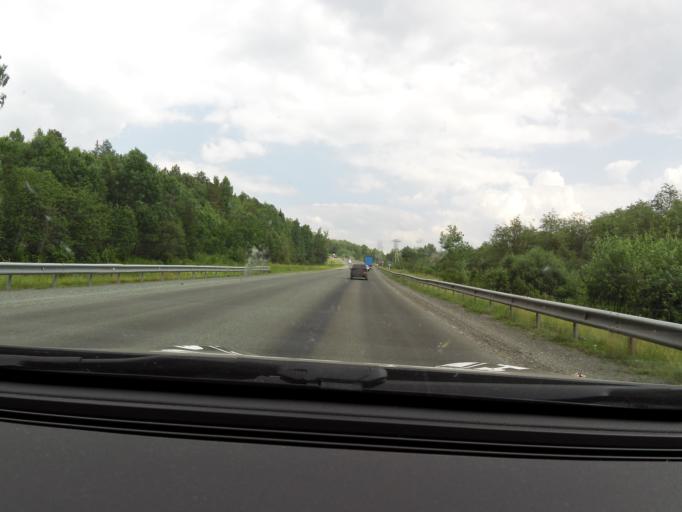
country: RU
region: Sverdlovsk
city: Ufimskiy
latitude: 56.7754
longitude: 58.2343
